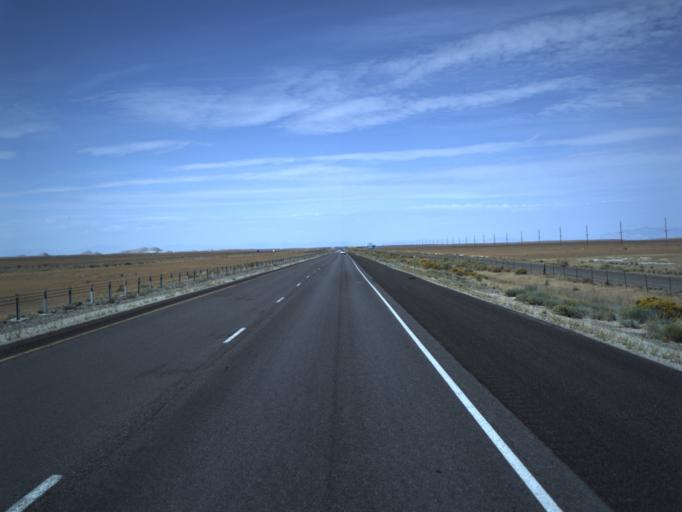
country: US
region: Utah
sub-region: Tooele County
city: Grantsville
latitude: 40.7260
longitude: -113.1462
